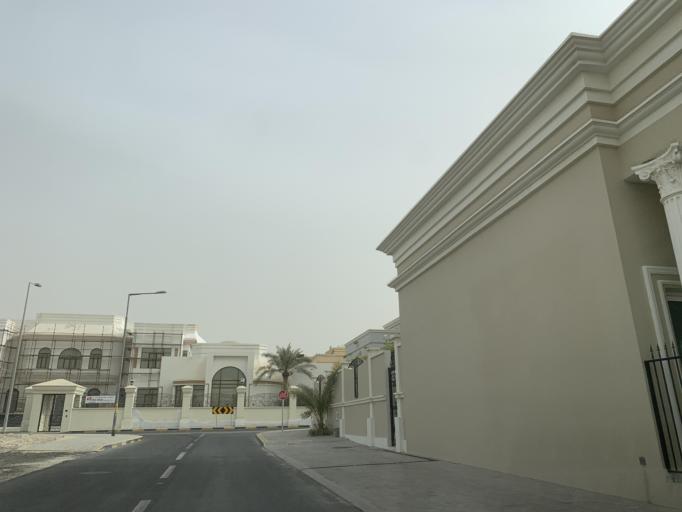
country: BH
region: Northern
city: Ar Rifa'
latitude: 26.1417
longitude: 50.5283
